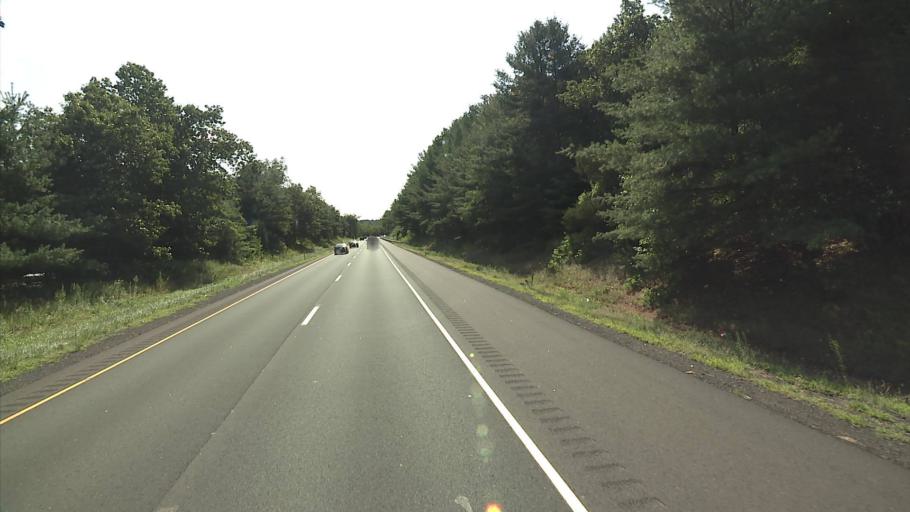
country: US
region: Connecticut
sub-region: Hartford County
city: Glastonbury Center
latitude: 41.7069
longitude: -72.5780
